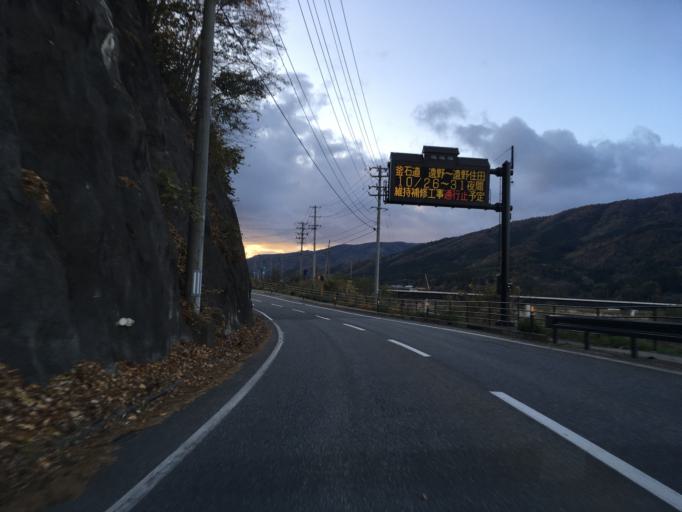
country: JP
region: Iwate
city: Tono
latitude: 39.3262
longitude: 141.5110
